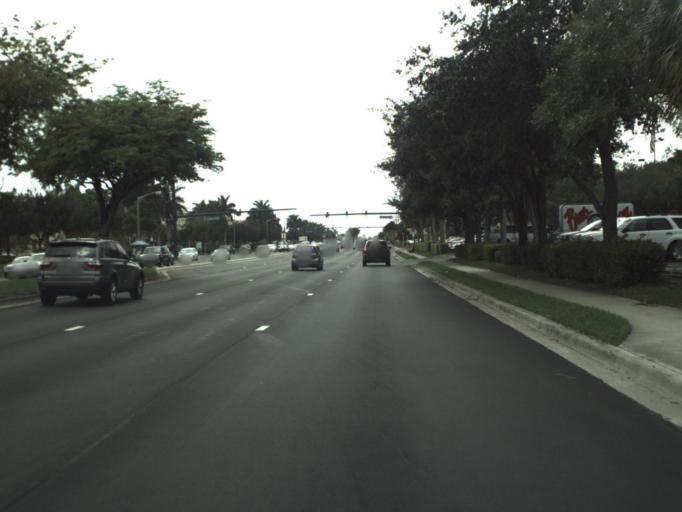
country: US
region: Florida
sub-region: Palm Beach County
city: Boynton Beach
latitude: 26.5392
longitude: -80.0908
